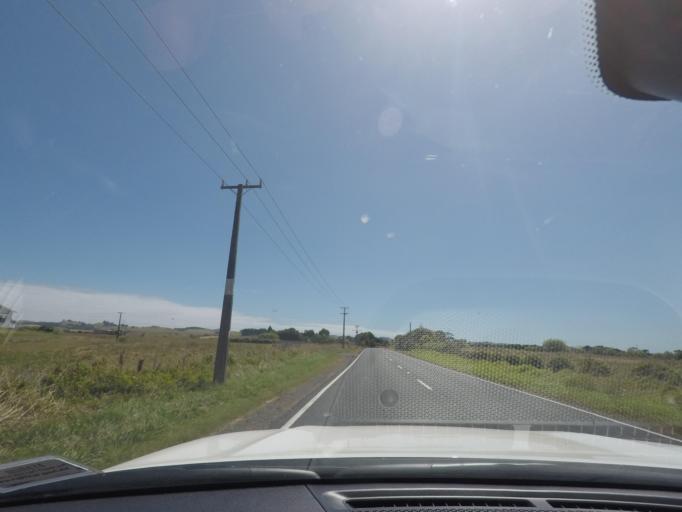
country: NZ
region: Auckland
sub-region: Auckland
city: Parakai
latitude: -36.6509
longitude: 174.4156
